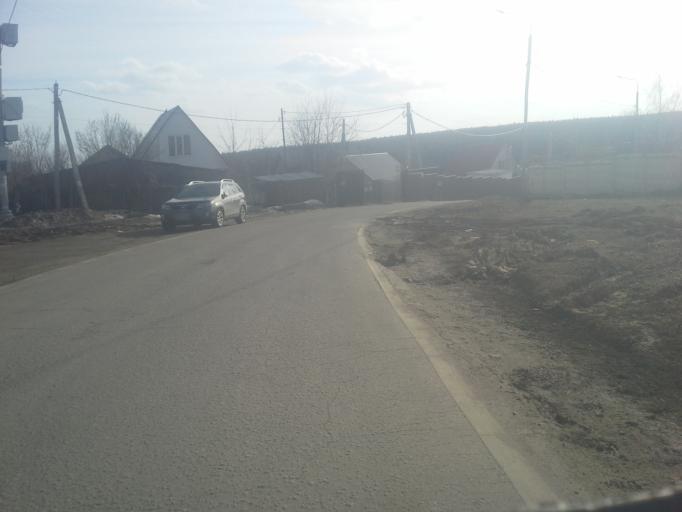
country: RU
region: Moskovskaya
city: Shcherbinka
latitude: 55.4660
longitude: 37.5391
